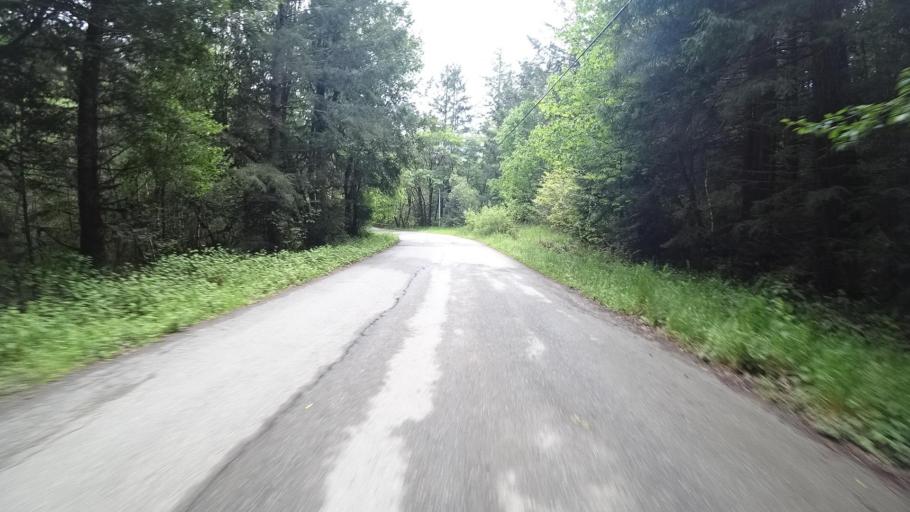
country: US
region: California
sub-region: Humboldt County
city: Blue Lake
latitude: 40.7819
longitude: -123.8786
